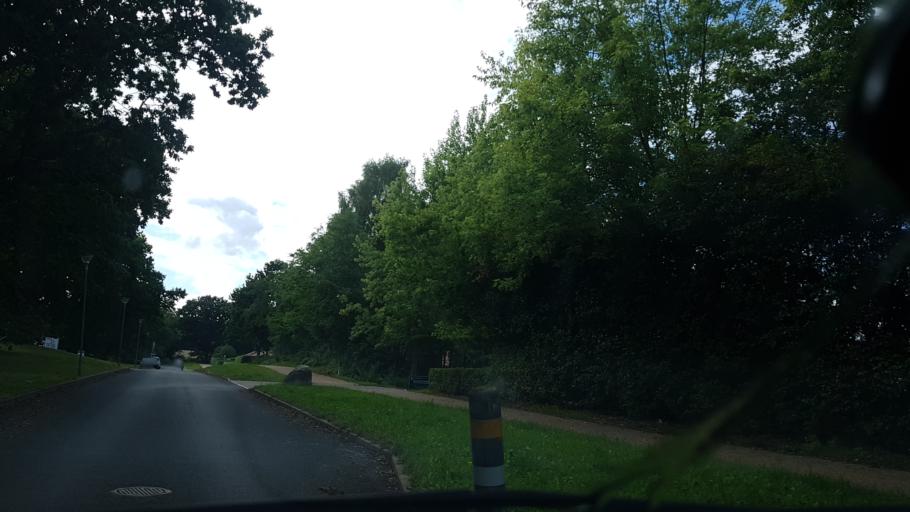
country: DK
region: Capital Region
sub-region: Fredensborg Kommune
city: Humlebaek
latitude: 55.9860
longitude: 12.5284
